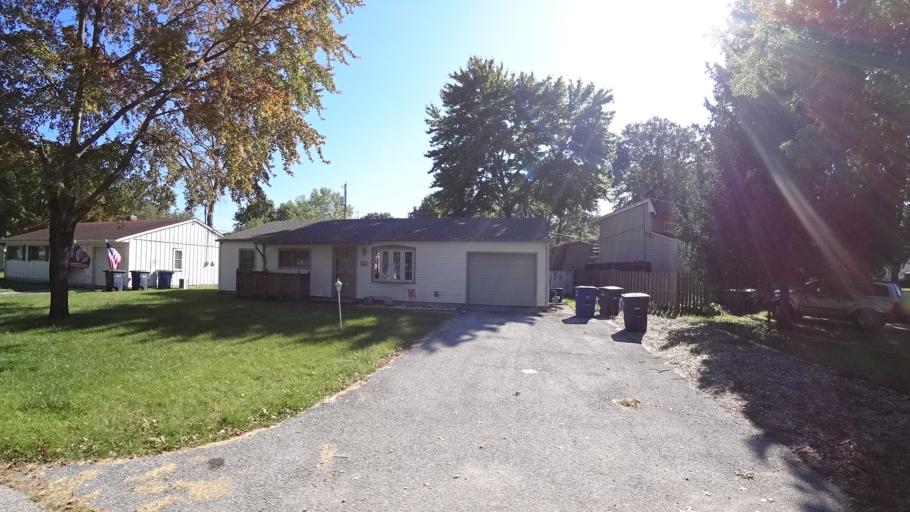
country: US
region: Indiana
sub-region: LaPorte County
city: Michigan City
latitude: 41.6918
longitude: -86.9020
